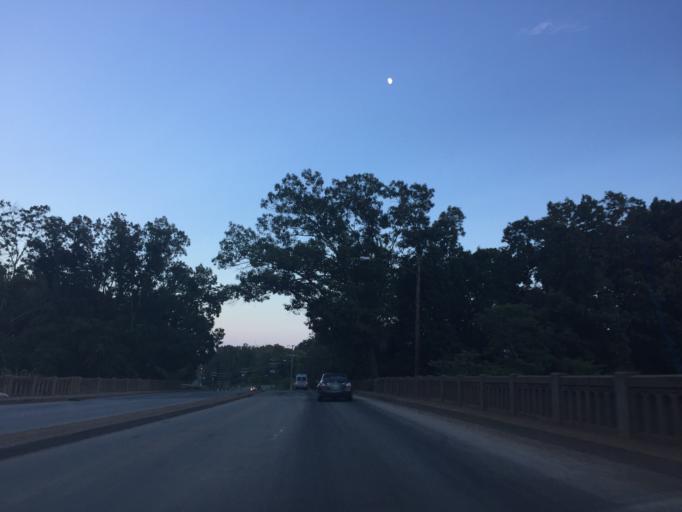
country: US
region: Virginia
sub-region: City of Charlottesville
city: Charlottesville
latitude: 38.0457
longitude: -78.4790
